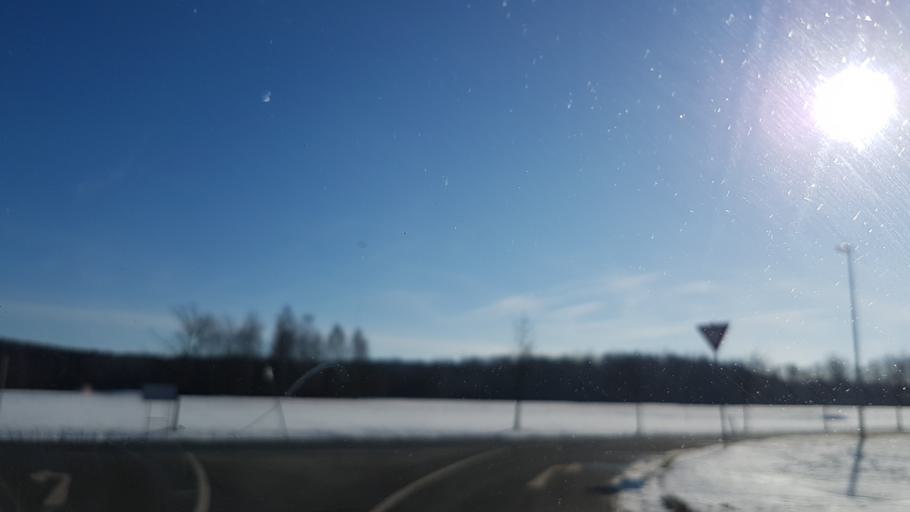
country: DE
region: Thuringia
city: Nobitz
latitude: 50.9750
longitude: 12.5174
